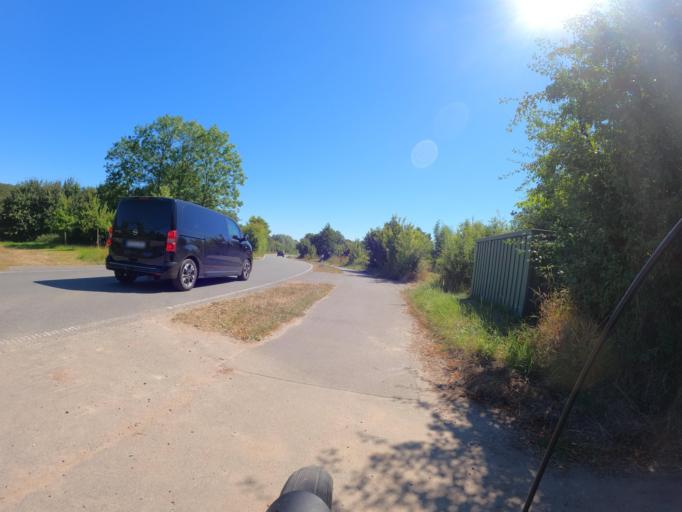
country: DE
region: Schleswig-Holstein
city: Dollerup
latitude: 54.7906
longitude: 9.7234
